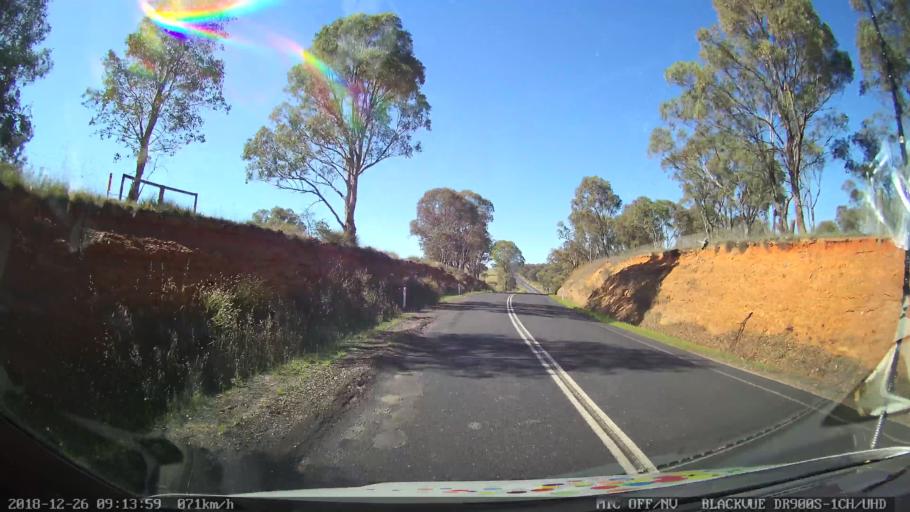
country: AU
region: New South Wales
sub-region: Mid-Western Regional
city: Kandos
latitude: -32.7736
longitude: 149.9798
